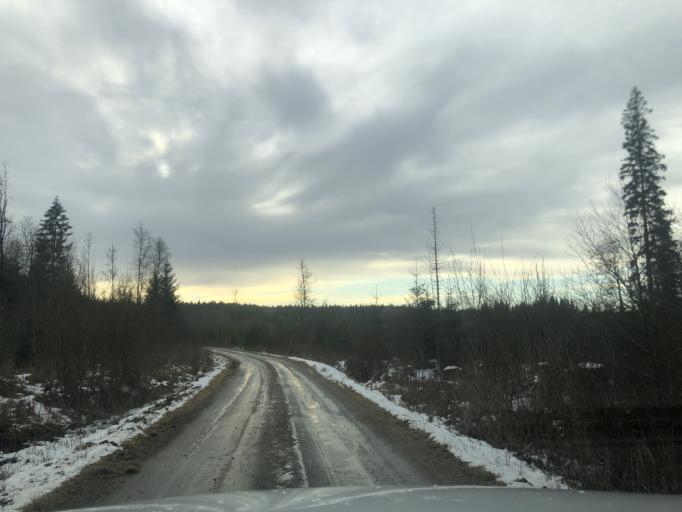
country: SE
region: Vaestra Goetaland
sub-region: Ulricehamns Kommun
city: Ulricehamn
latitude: 57.7914
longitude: 13.4853
